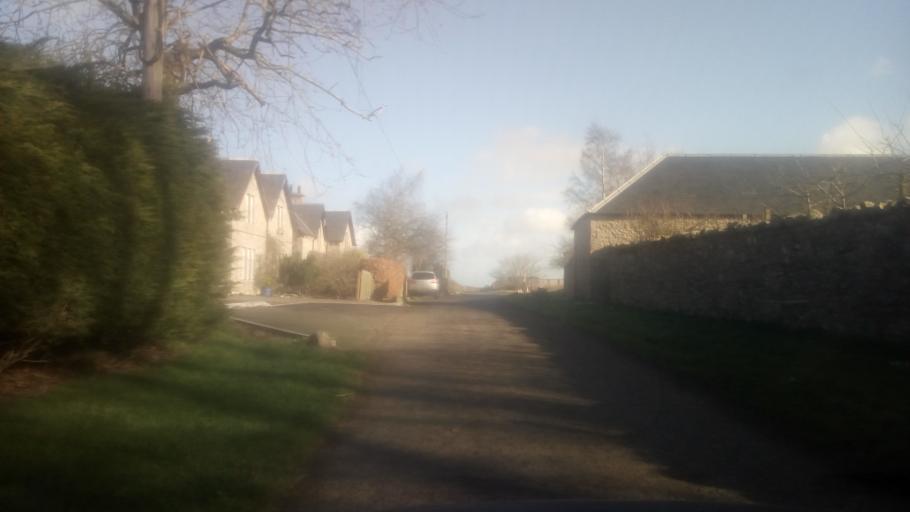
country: GB
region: Scotland
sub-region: The Scottish Borders
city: Jedburgh
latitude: 55.4902
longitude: -2.5231
